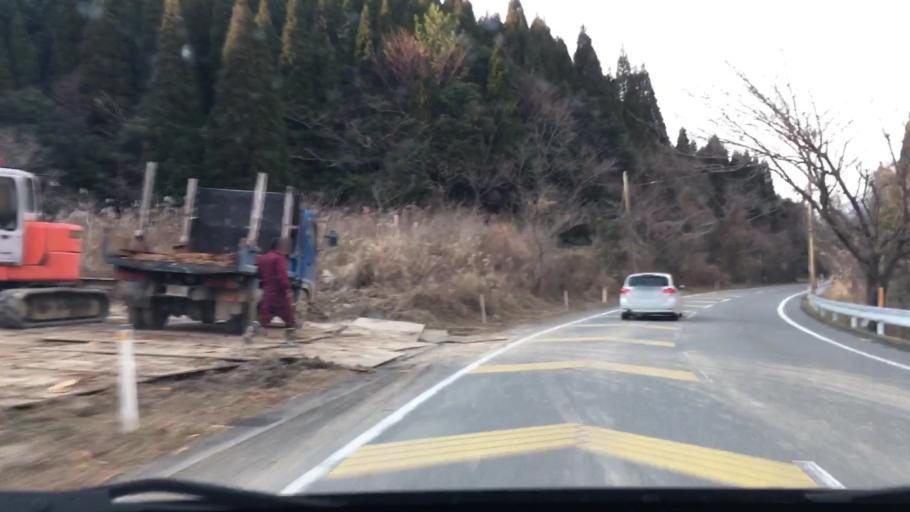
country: JP
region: Miyazaki
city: Miyazaki-shi
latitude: 31.7906
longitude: 131.3159
